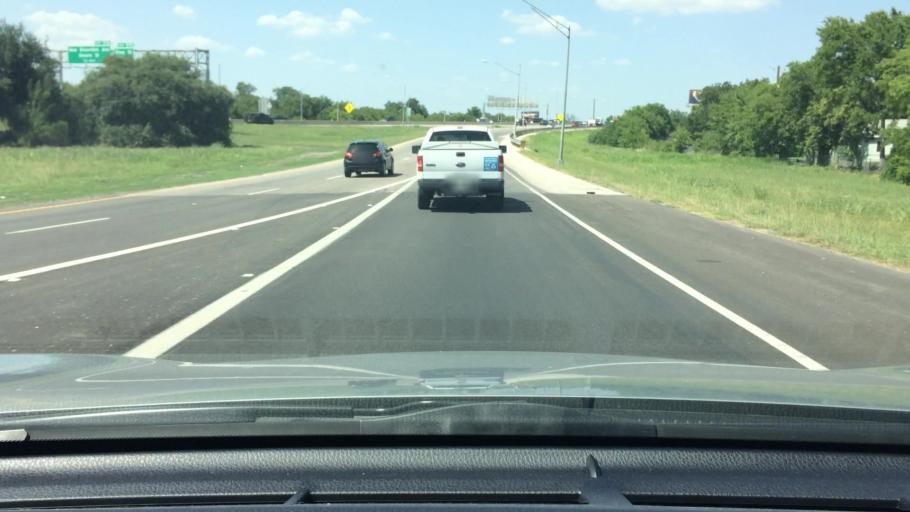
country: US
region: Texas
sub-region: Bexar County
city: San Antonio
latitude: 29.3957
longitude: -98.4757
